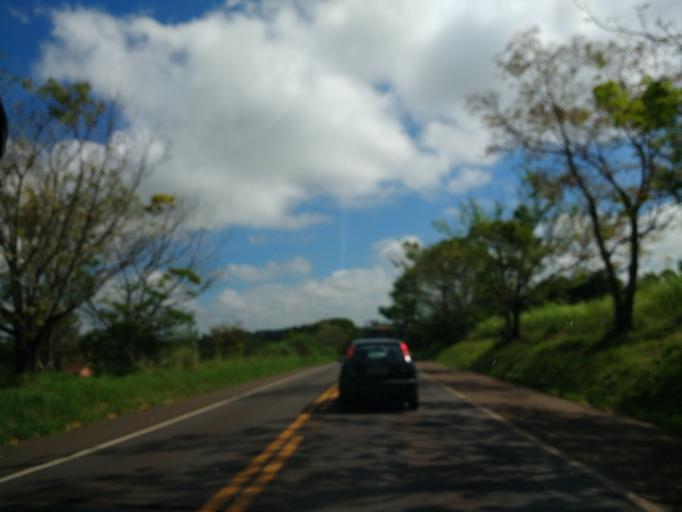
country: BR
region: Parana
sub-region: Cruzeiro Do Oeste
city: Cruzeiro do Oeste
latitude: -23.7687
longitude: -53.1761
